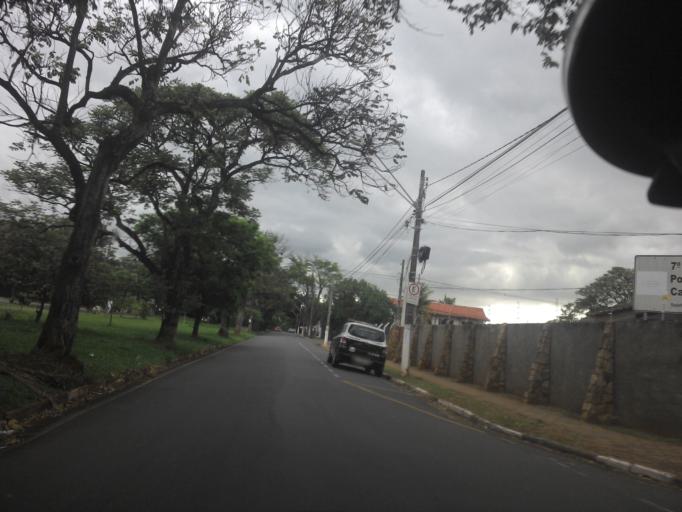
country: BR
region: Sao Paulo
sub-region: Campinas
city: Campinas
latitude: -22.8196
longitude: -47.0743
